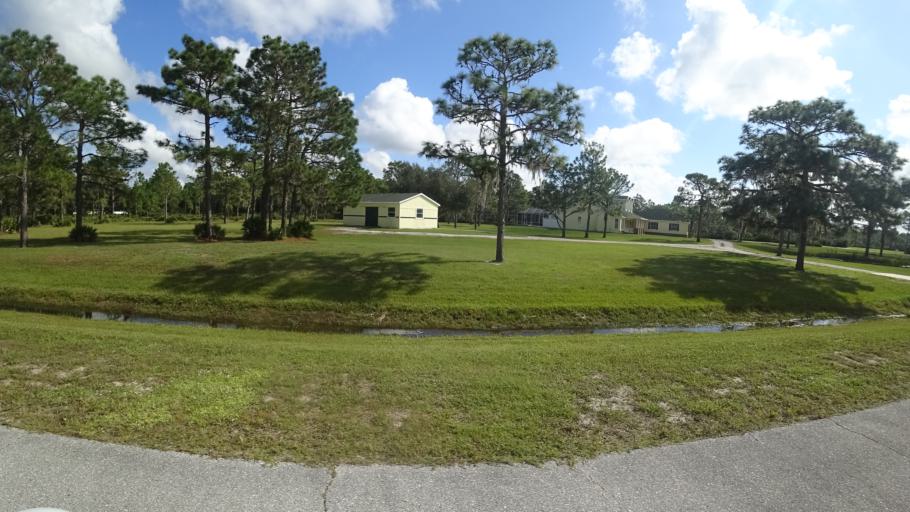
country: US
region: Florida
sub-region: Sarasota County
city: The Meadows
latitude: 27.3993
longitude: -82.3397
